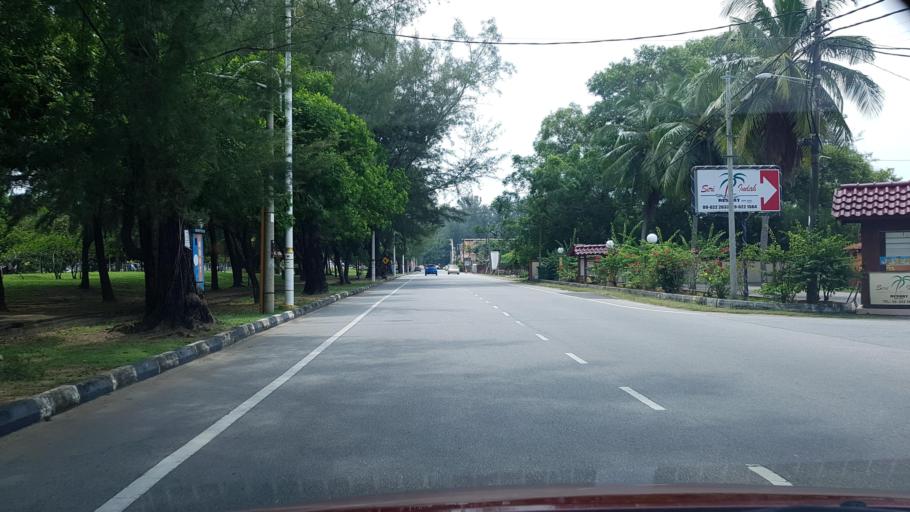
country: MY
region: Terengganu
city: Kuala Terengganu
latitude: 5.3183
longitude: 103.1562
